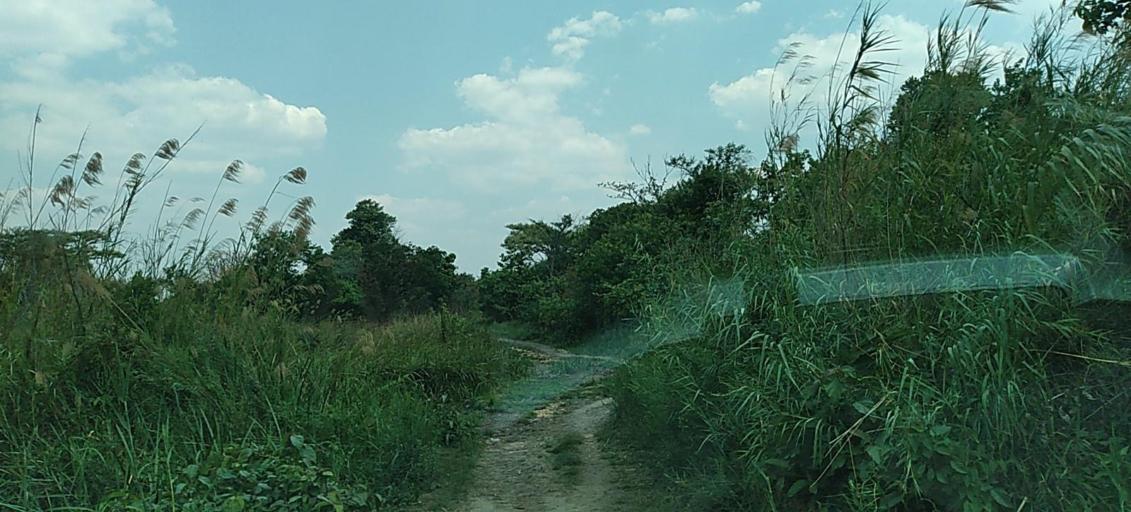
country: CD
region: Katanga
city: Kipushi
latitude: -11.9946
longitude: 27.4183
